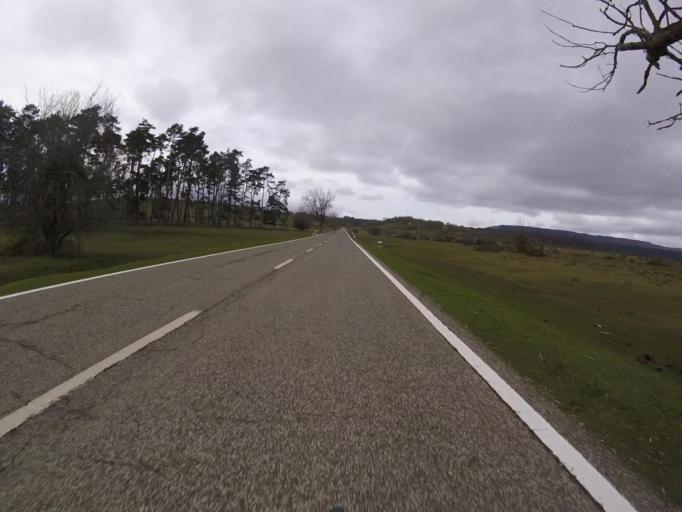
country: ES
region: Navarre
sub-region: Provincia de Navarra
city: Eulate
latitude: 42.8122
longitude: -2.1613
